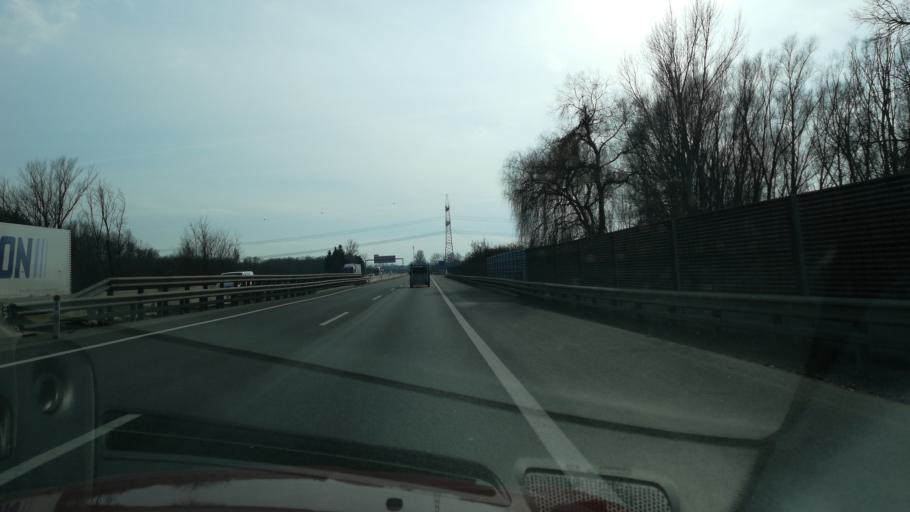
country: AT
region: Lower Austria
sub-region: Politischer Bezirk Sankt Polten
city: Traismauer
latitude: 48.3318
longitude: 15.7214
